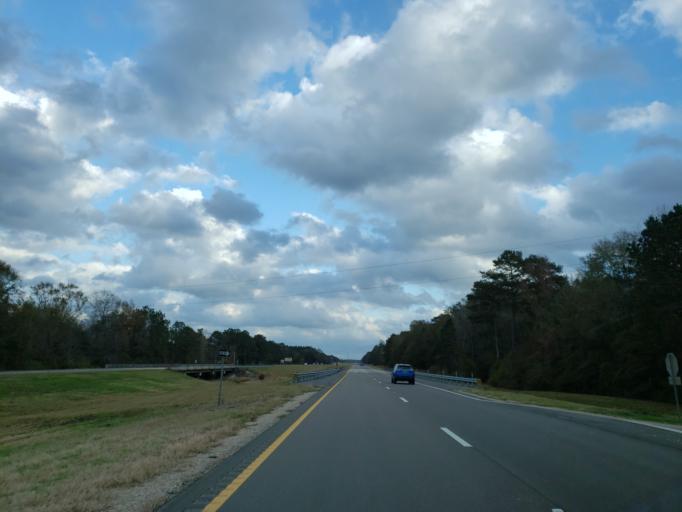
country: US
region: Mississippi
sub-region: Perry County
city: New Augusta
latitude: 31.2069
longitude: -89.0819
